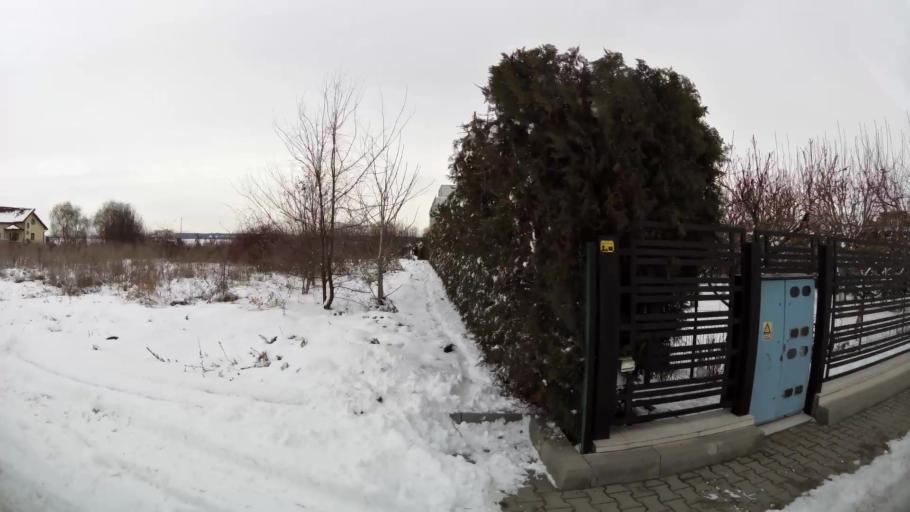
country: RO
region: Ilfov
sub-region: Voluntari City
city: Voluntari
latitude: 44.5108
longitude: 26.1423
